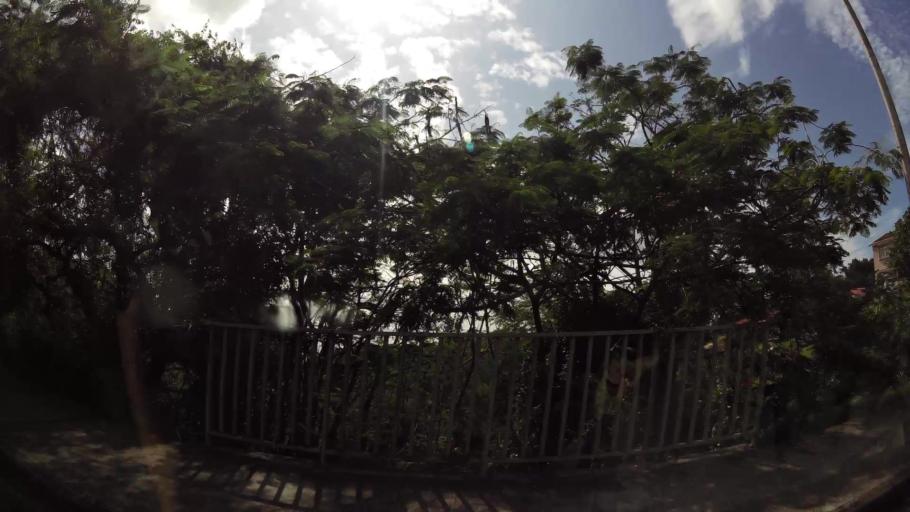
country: GP
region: Guadeloupe
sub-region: Guadeloupe
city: Basse-Terre
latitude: 16.0052
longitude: -61.7305
